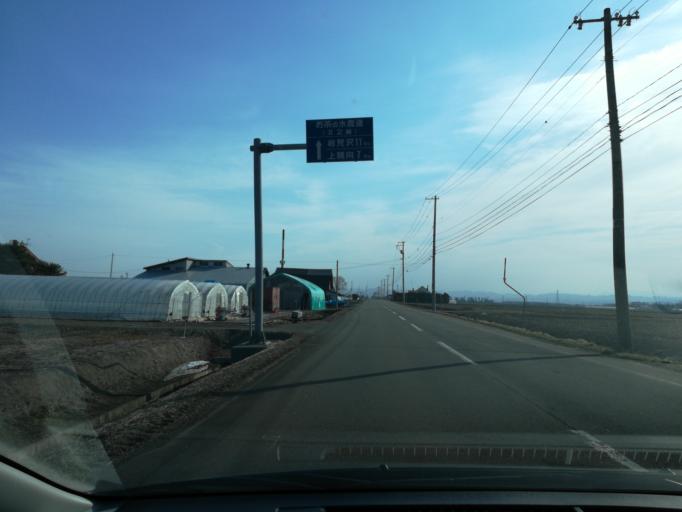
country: JP
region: Hokkaido
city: Iwamizawa
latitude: 43.1637
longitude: 141.6548
